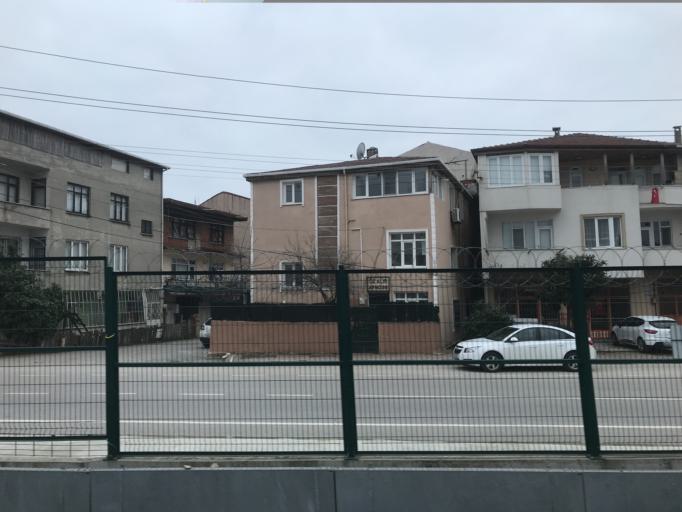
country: TR
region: Kocaeli
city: Darica
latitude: 40.7920
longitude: 29.3908
